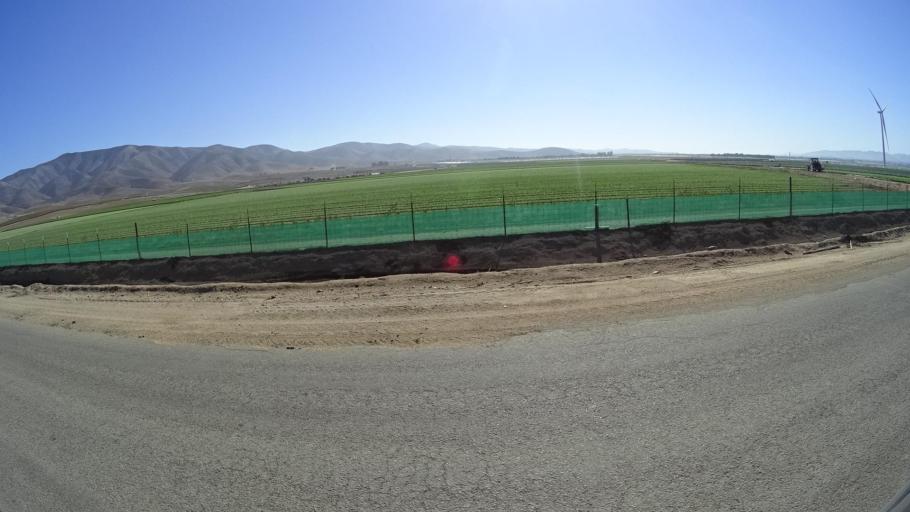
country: US
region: California
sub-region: Monterey County
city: Soledad
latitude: 36.4653
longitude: -121.3537
